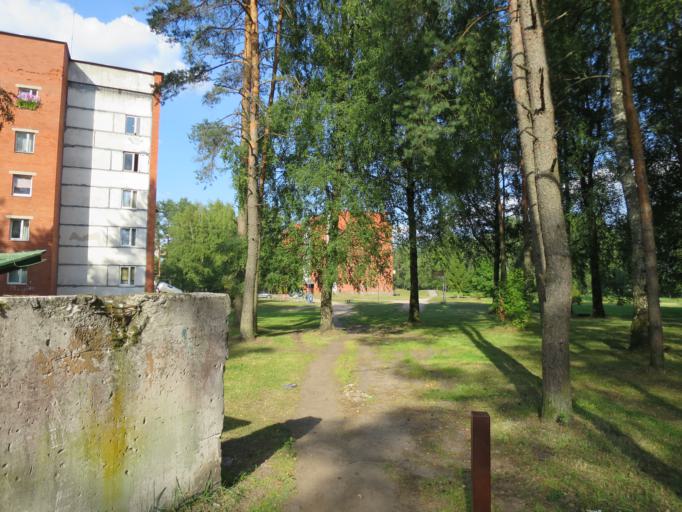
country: LV
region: Incukalns
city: Vangazi
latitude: 57.0888
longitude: 24.5459
